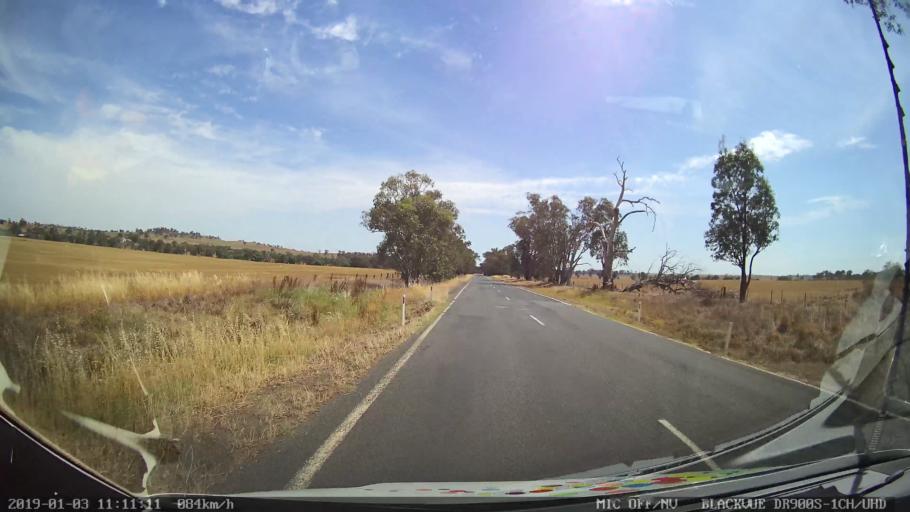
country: AU
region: New South Wales
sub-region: Young
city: Young
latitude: -34.2179
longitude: 148.2594
